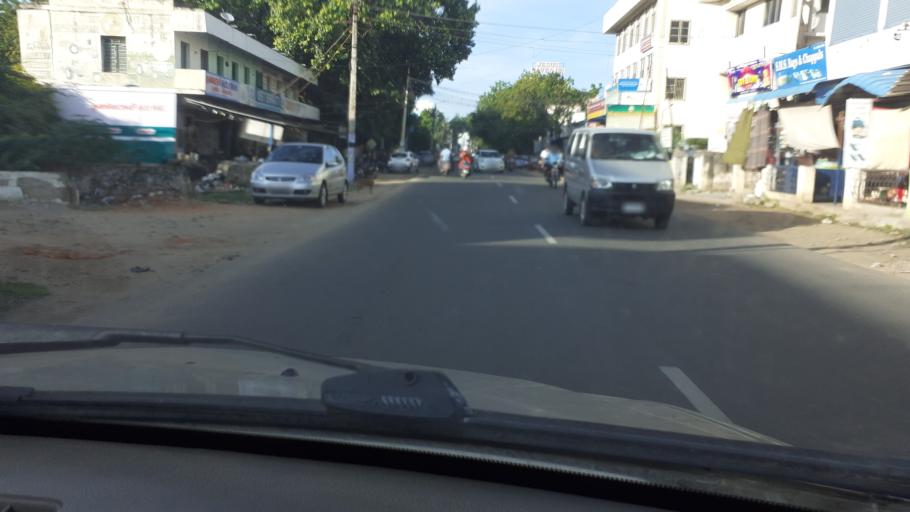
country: IN
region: Tamil Nadu
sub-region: Tirunelveli Kattabo
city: Tirunelveli
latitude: 8.7136
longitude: 77.7321
